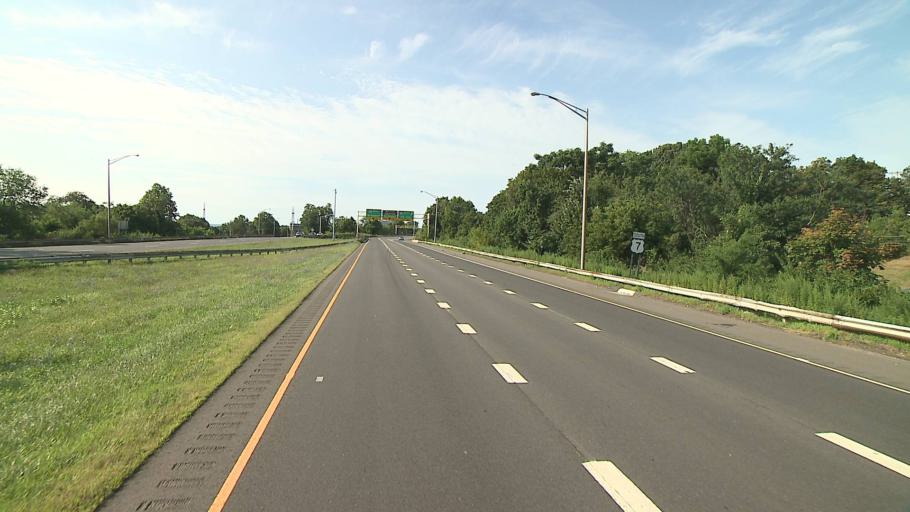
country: US
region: Connecticut
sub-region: Fairfield County
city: Norwalk
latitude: 41.1112
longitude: -73.4191
